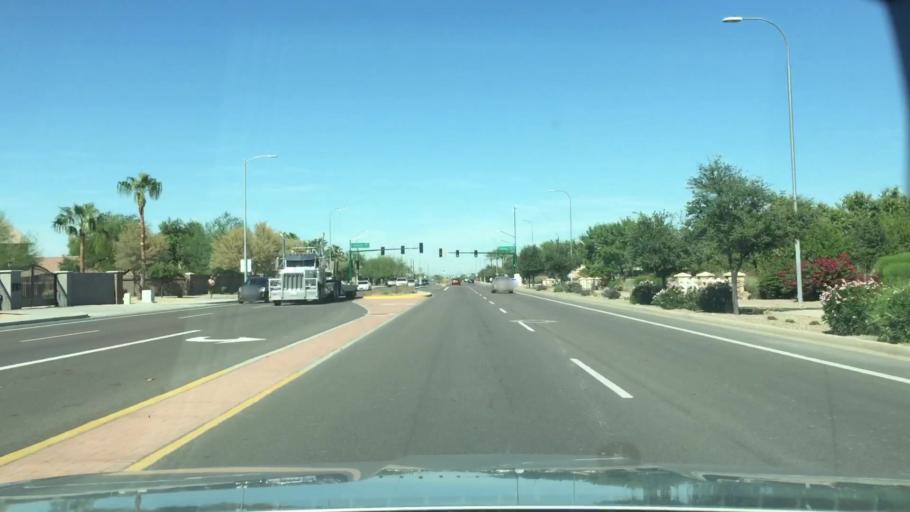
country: US
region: Arizona
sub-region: Maricopa County
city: Laveen
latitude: 33.3835
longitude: -112.1337
